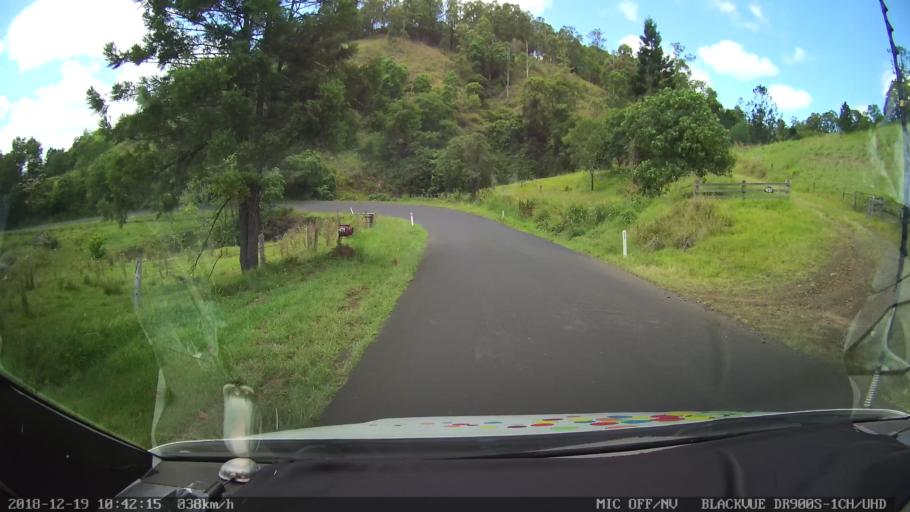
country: AU
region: New South Wales
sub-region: Lismore Municipality
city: Nimbin
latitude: -28.5918
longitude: 153.1666
